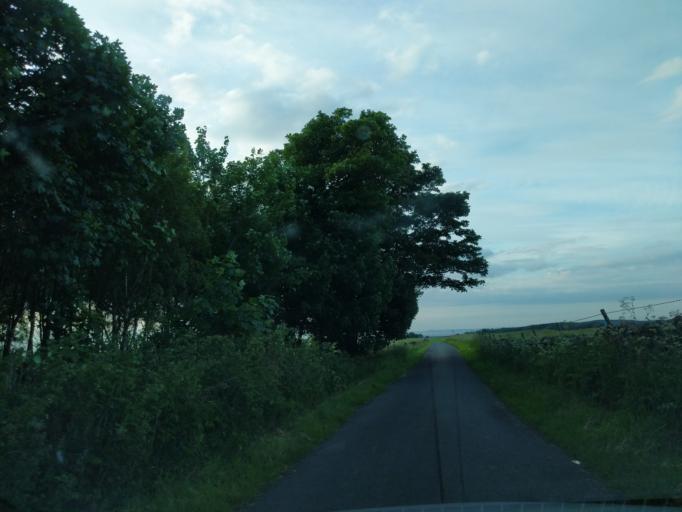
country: GB
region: Scotland
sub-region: Midlothian
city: Gorebridge
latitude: 55.7868
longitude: -3.0964
